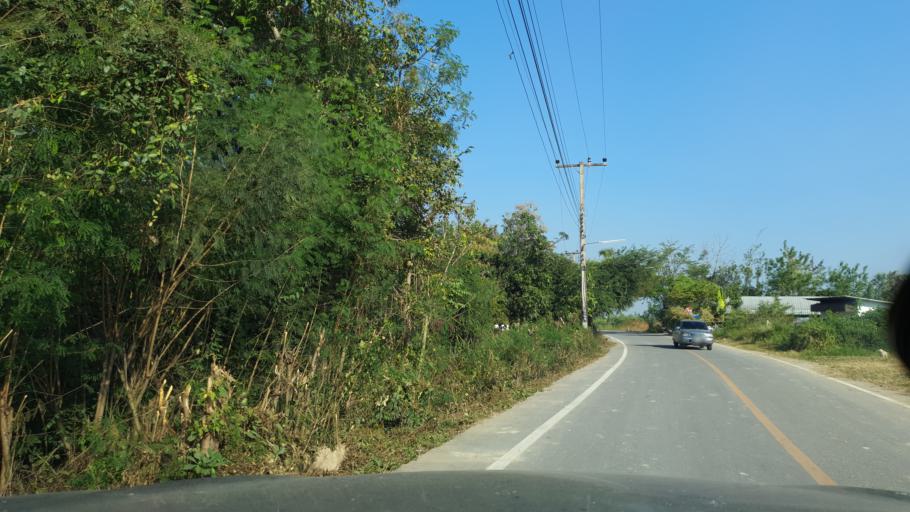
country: TH
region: Lamphun
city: Ban Thi
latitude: 18.6826
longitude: 99.1190
